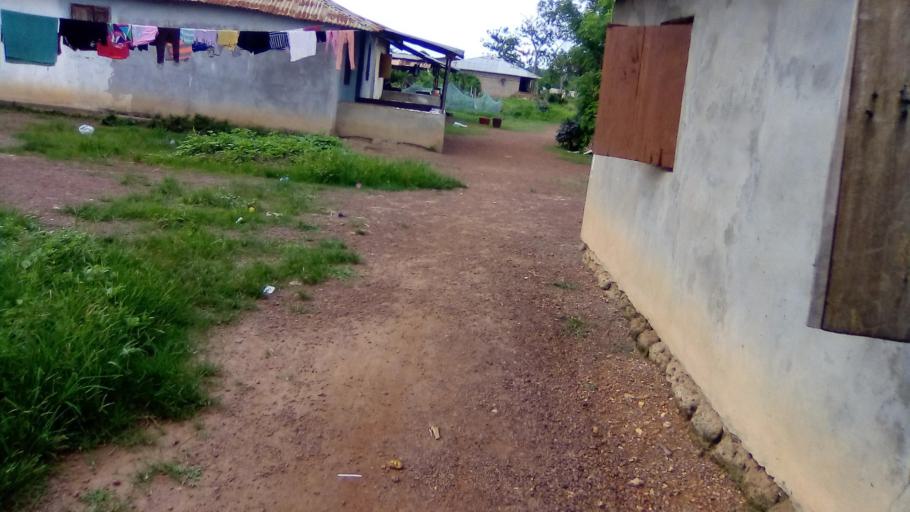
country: SL
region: Southern Province
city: Largo
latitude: 8.1110
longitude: -12.0680
